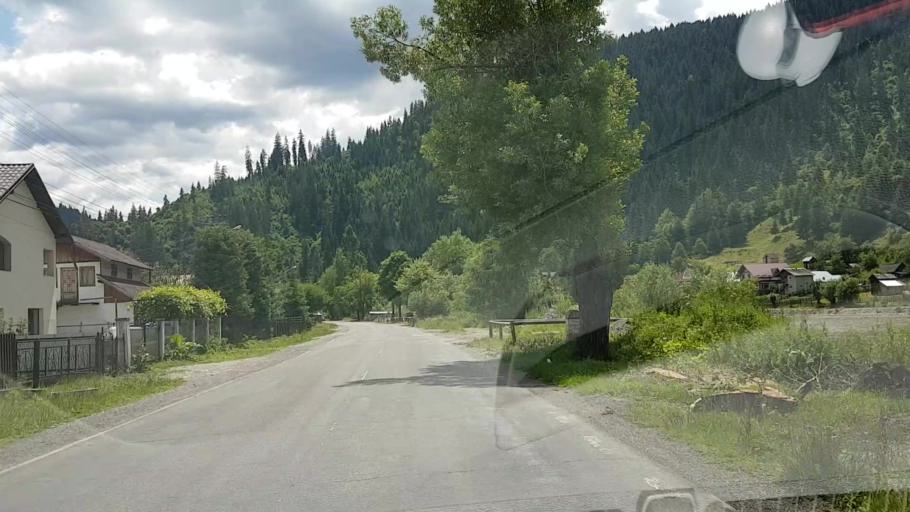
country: RO
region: Suceava
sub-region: Comuna Brosteni
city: Brosteni
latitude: 47.2428
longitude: 25.6910
